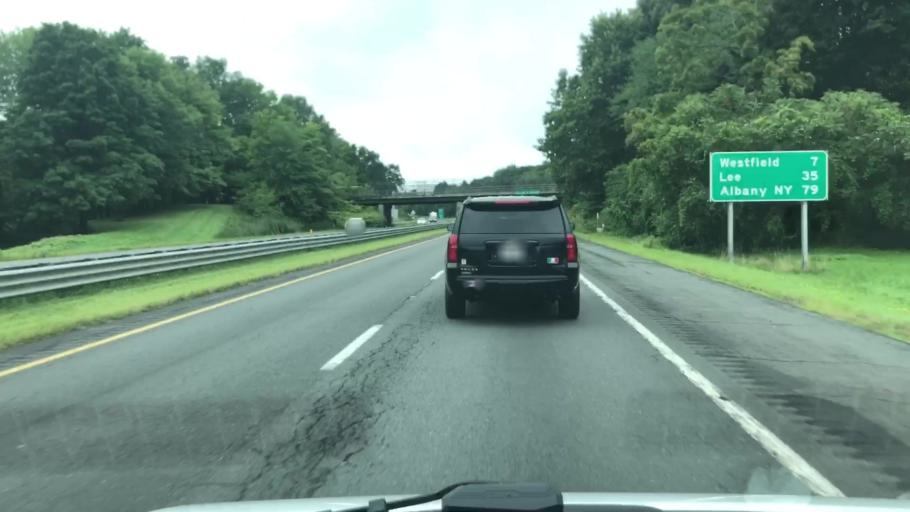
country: US
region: Massachusetts
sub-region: Hampden County
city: Chicopee
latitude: 42.1533
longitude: -72.6518
